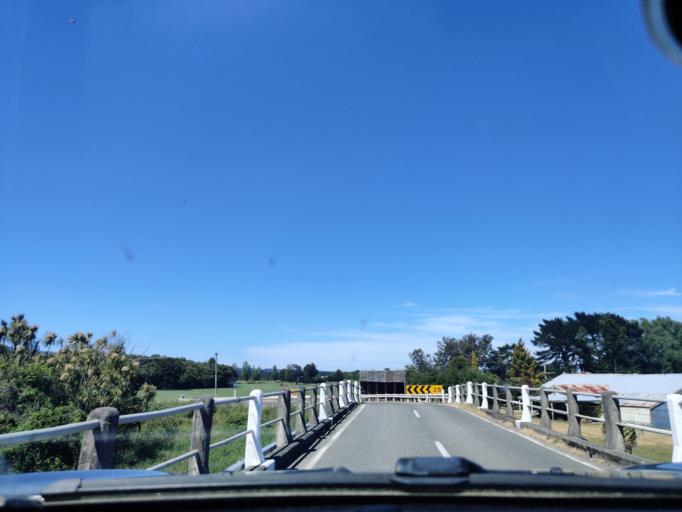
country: NZ
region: Wellington
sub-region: Upper Hutt City
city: Upper Hutt
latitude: -41.2868
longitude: 175.2685
